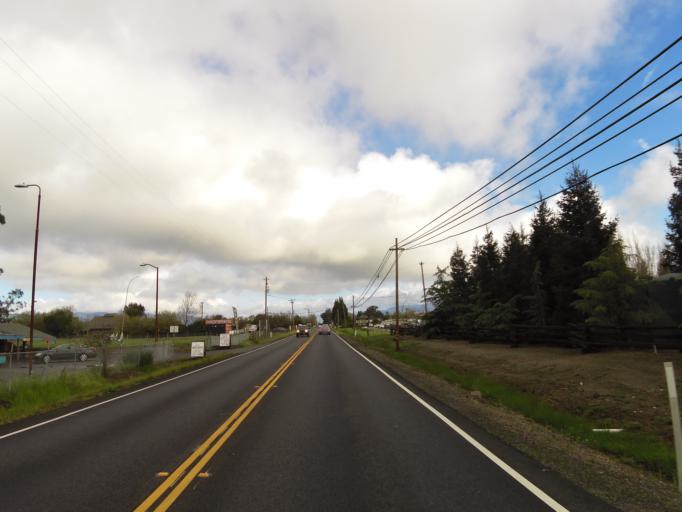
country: US
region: California
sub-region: Sonoma County
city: Temelec
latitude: 38.2214
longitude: -122.4560
